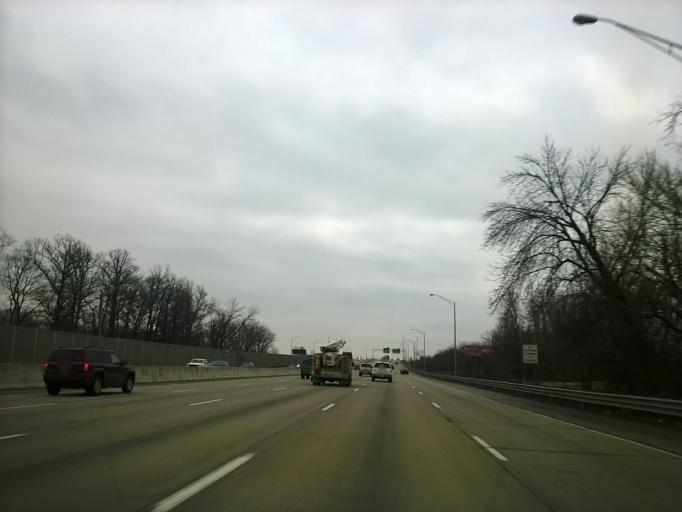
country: US
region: Indiana
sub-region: Marion County
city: Lawrence
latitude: 39.8403
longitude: -86.0406
